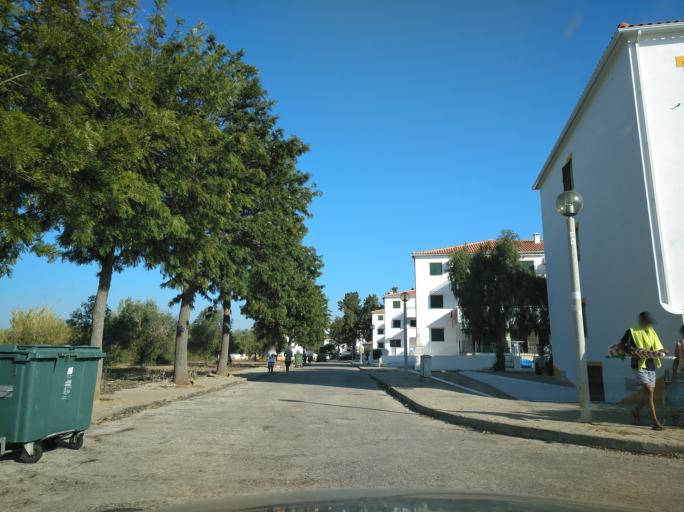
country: PT
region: Faro
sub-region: Vila Real de Santo Antonio
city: Monte Gordo
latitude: 37.1726
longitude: -7.5064
